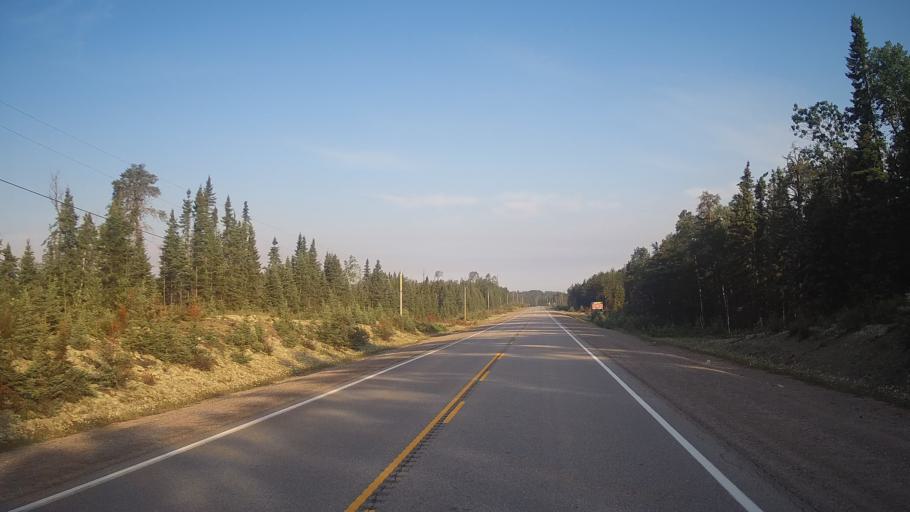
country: CA
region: Ontario
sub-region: Rainy River District
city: Atikokan
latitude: 49.3480
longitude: -91.5060
